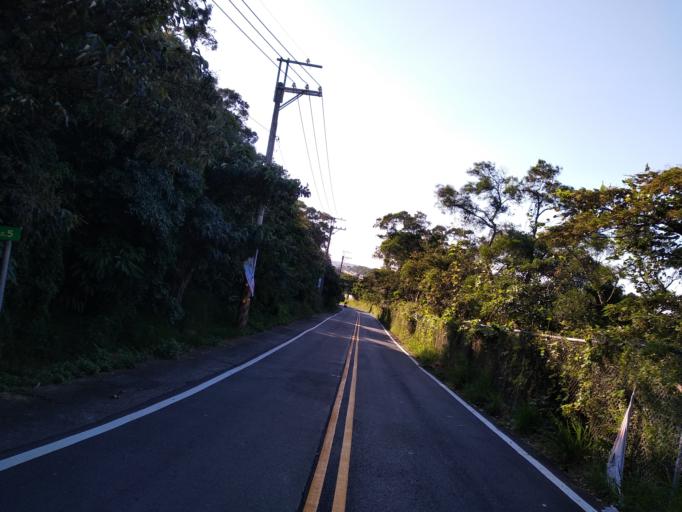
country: TW
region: Taiwan
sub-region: Hsinchu
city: Zhubei
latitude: 24.8757
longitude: 121.0551
